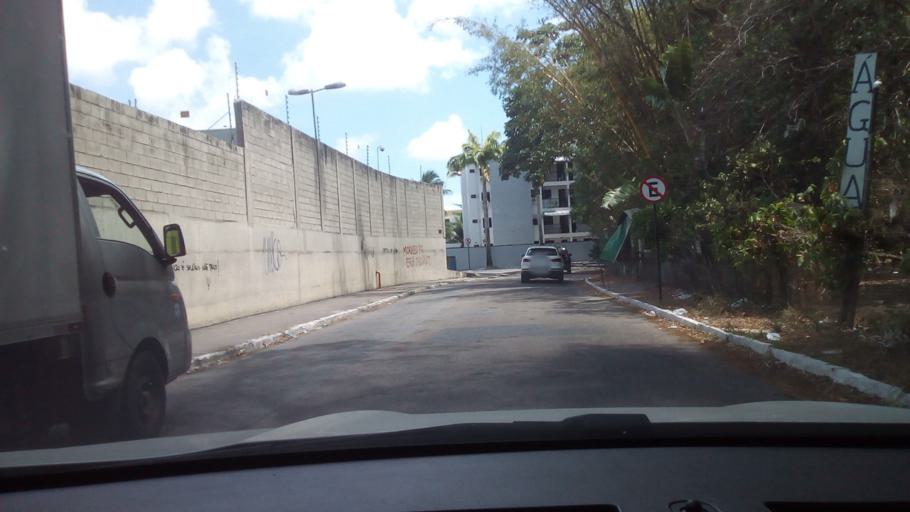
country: BR
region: Paraiba
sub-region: Joao Pessoa
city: Joao Pessoa
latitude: -7.1475
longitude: -34.8495
